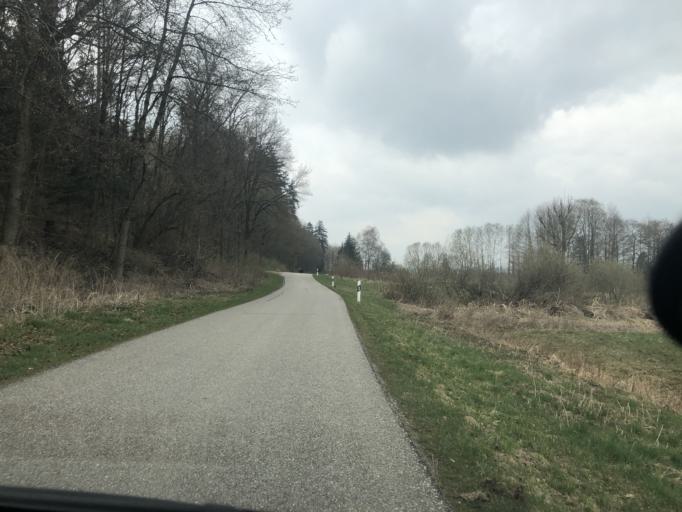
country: DE
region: Bavaria
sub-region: Upper Bavaria
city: Wolfersdorf
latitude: 48.4421
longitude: 11.7086
